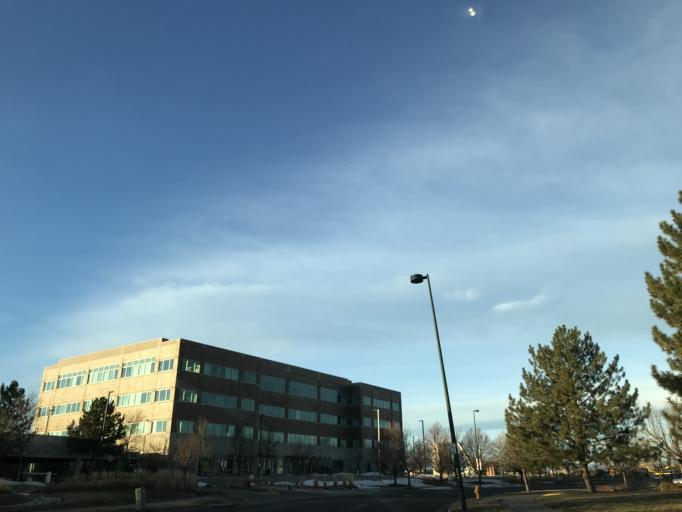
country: US
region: Colorado
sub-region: Arapahoe County
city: Glendale
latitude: 39.7185
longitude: -104.9015
